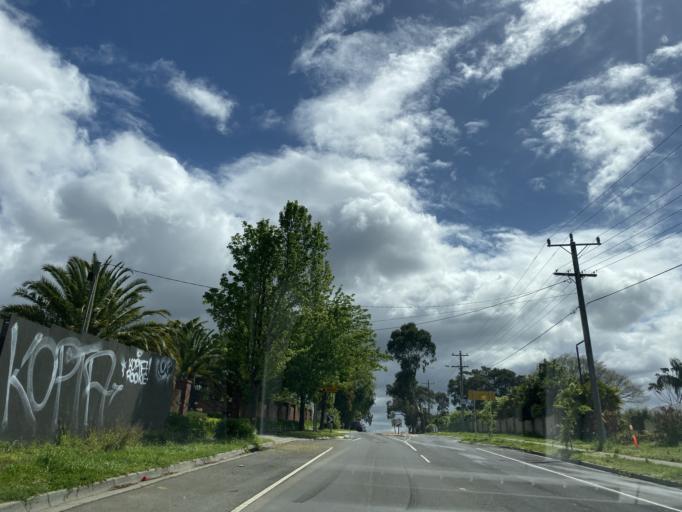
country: AU
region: Victoria
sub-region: Manningham
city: Doncaster East
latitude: -37.7671
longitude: 145.1414
